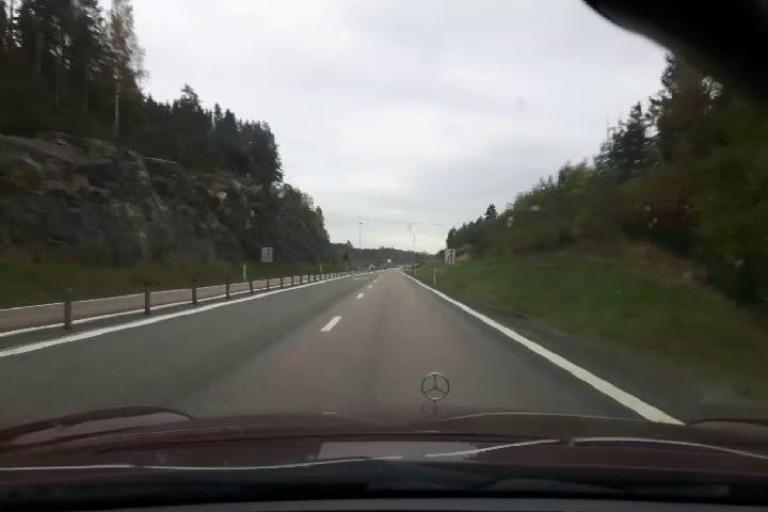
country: SE
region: Vaesternorrland
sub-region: Kramfors Kommun
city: Nordingra
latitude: 62.9244
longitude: 18.0990
